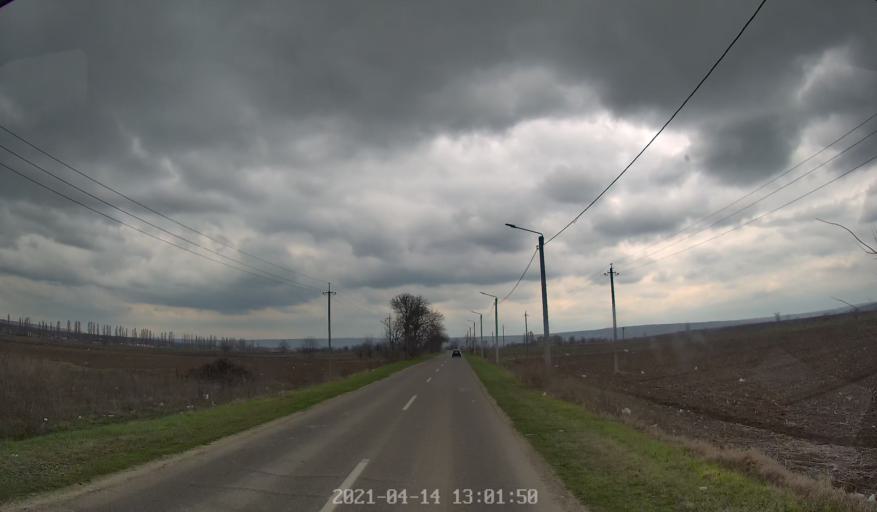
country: MD
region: Chisinau
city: Vadul lui Voda
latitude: 47.1284
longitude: 29.1139
